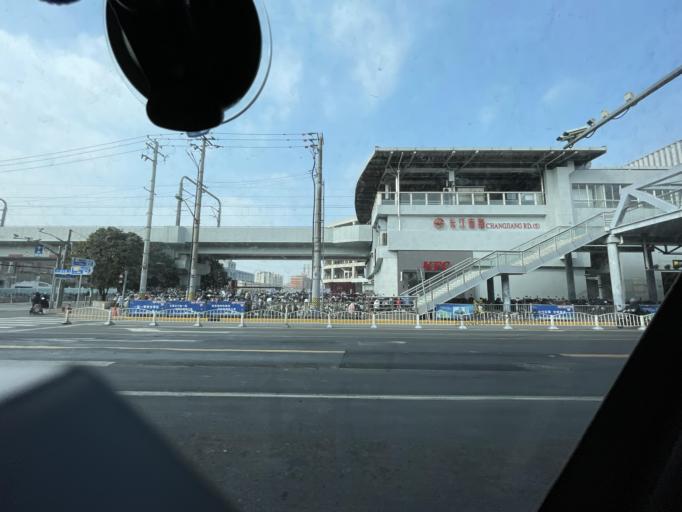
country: CN
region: Shanghai Shi
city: Baoshan
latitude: 31.3333
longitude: 121.4869
